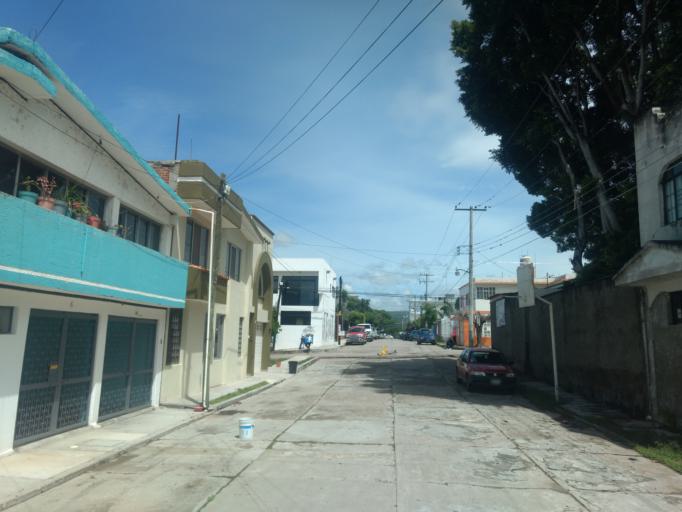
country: MX
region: Oaxaca
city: Ciudad de Huajuapam de Leon
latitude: 17.8019
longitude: -97.7772
